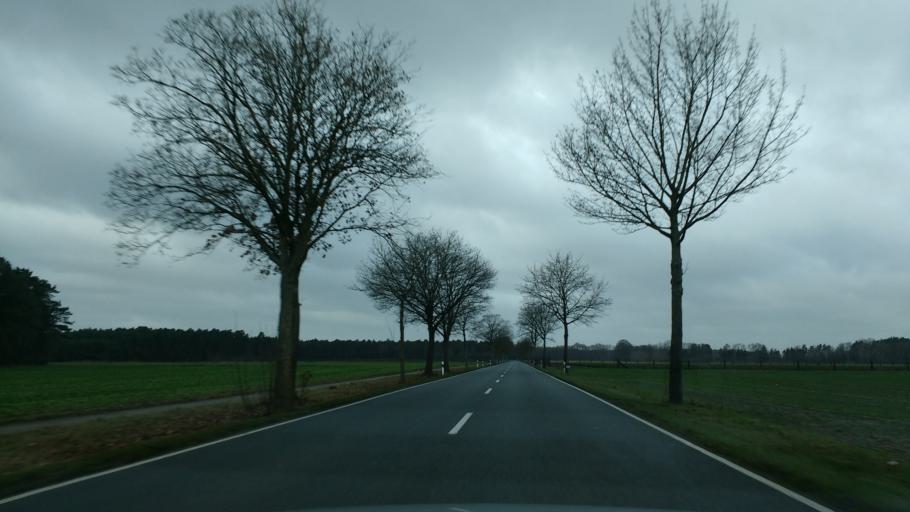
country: DE
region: Lower Saxony
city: Wietze
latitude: 52.6617
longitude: 9.7570
